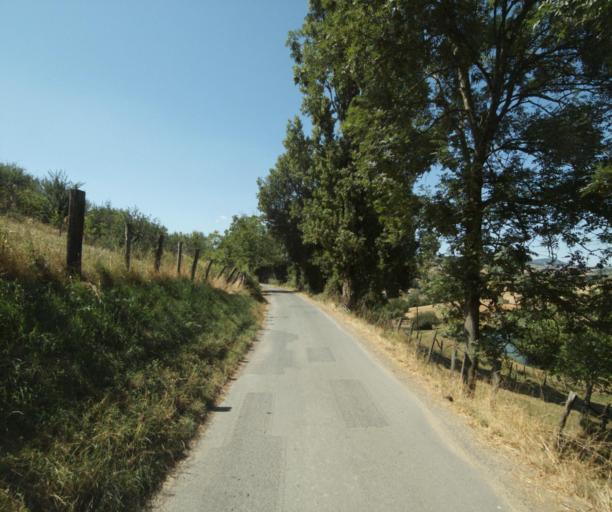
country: FR
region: Rhone-Alpes
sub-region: Departement du Rhone
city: Courzieu
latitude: 45.7302
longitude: 4.5338
